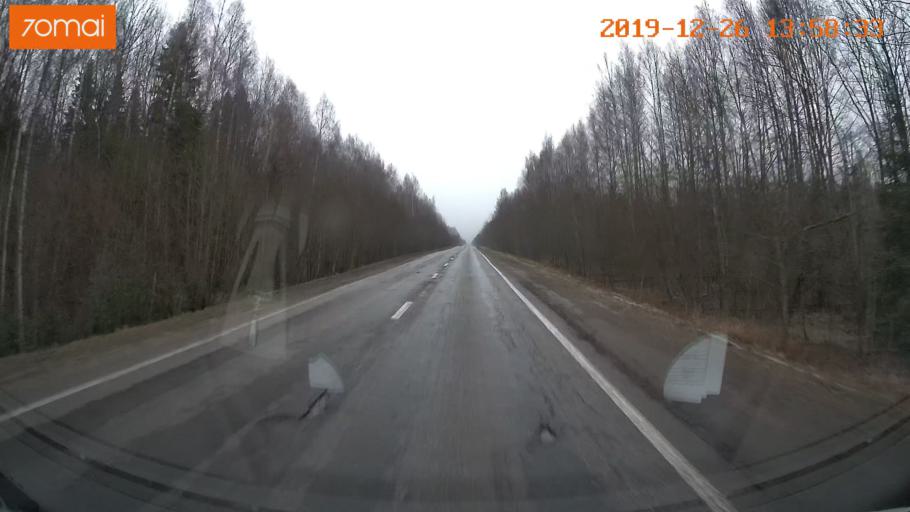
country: RU
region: Jaroslavl
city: Poshekhon'ye
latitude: 58.5731
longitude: 38.7034
